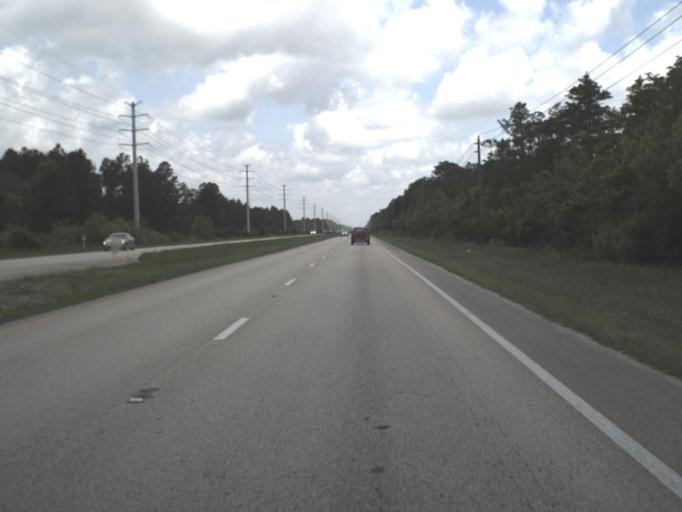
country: US
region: Florida
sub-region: Saint Johns County
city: Villano Beach
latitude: 30.0338
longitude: -81.4111
